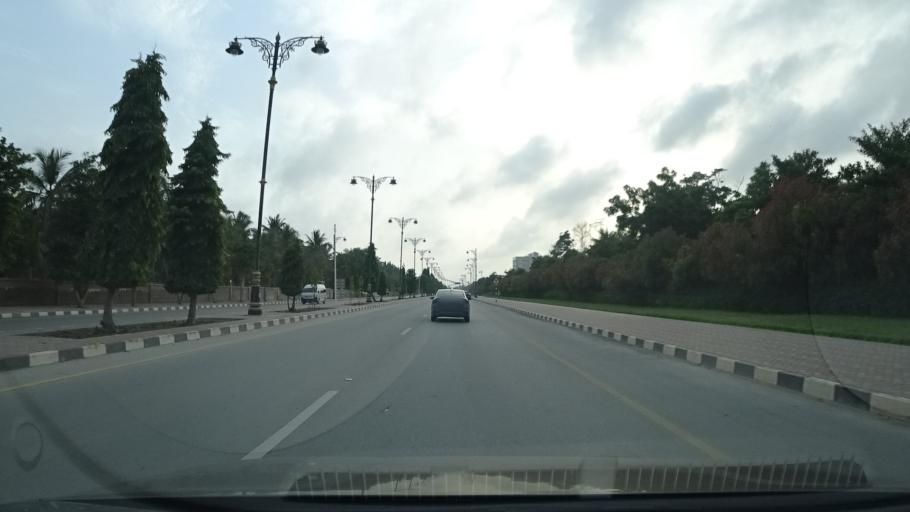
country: OM
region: Zufar
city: Salalah
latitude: 17.0260
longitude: 54.1650
